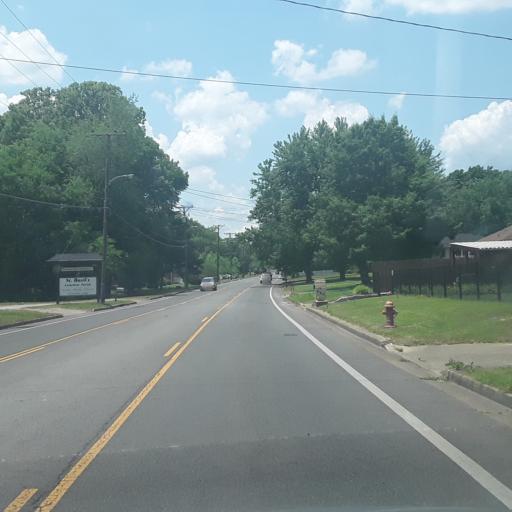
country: US
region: Tennessee
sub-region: Williamson County
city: Brentwood Estates
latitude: 36.0592
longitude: -86.7099
